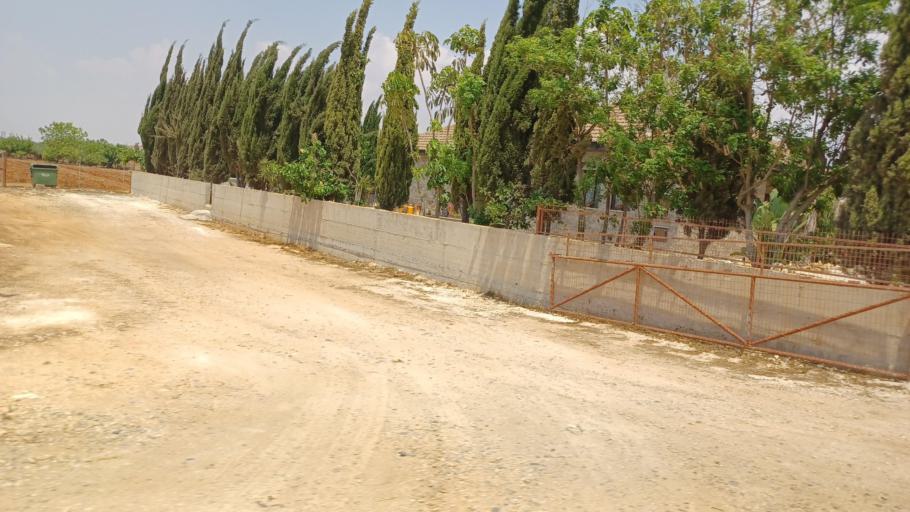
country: CY
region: Ammochostos
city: Liopetri
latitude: 34.9915
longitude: 33.8515
